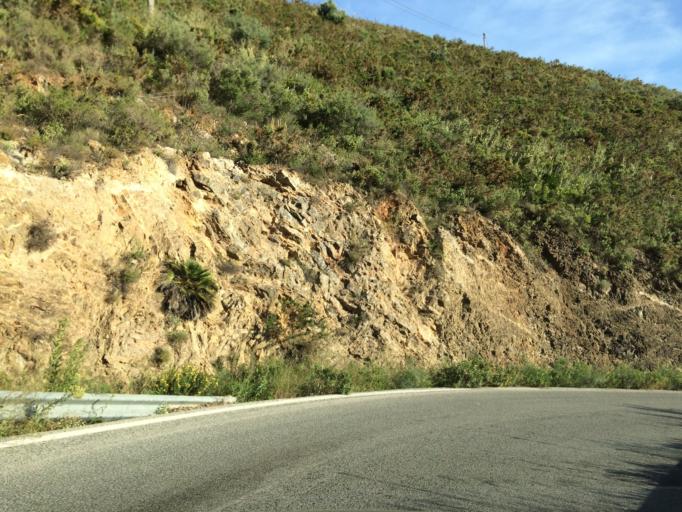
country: ES
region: Andalusia
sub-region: Provincia de Malaga
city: Totalan
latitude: 36.7426
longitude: -4.3300
